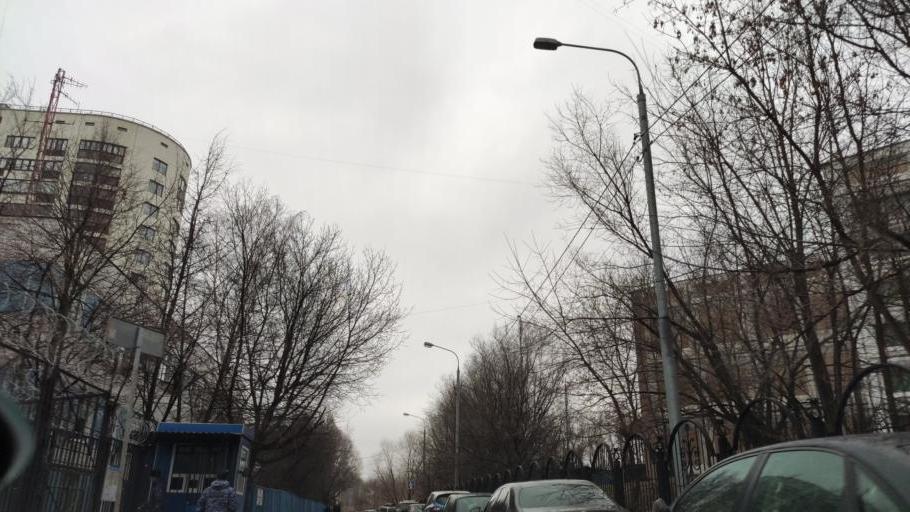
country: RU
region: Moskovskaya
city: Bol'shaya Setun'
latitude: 55.7454
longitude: 37.4278
